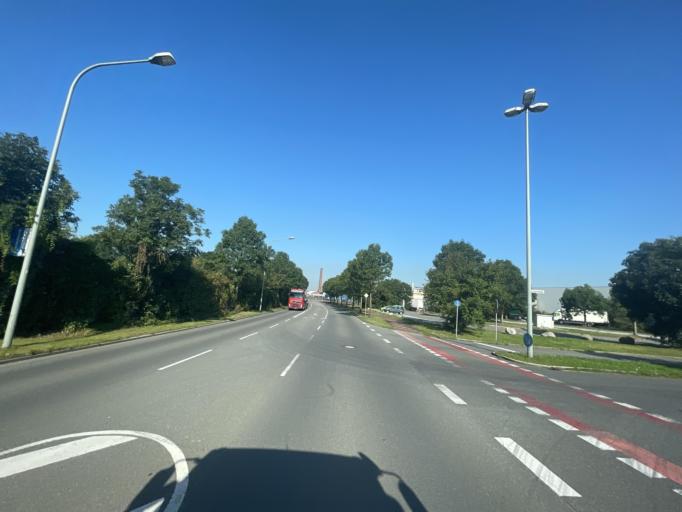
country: DE
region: North Rhine-Westphalia
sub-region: Regierungsbezirk Dusseldorf
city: Meerbusch
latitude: 51.3335
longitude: 6.6742
